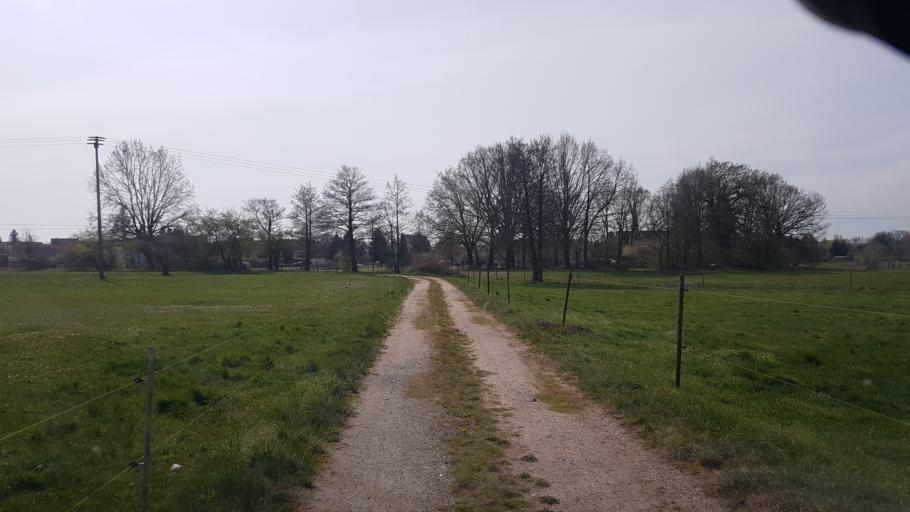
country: DE
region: Brandenburg
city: Doberlug-Kirchhain
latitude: 51.6159
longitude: 13.5486
